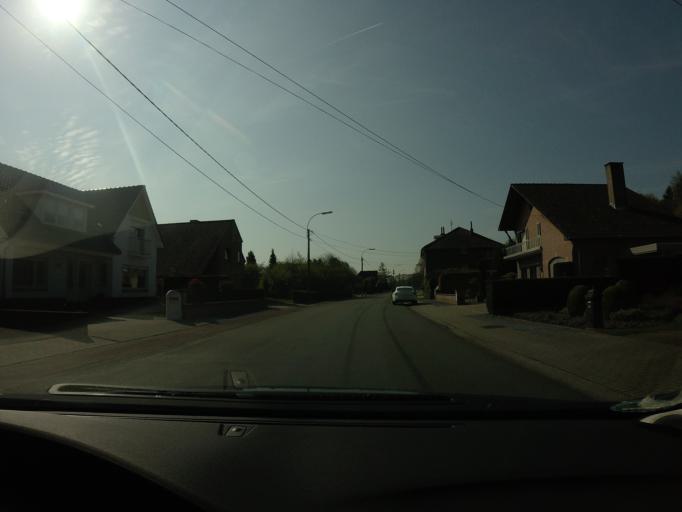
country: BE
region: Flanders
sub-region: Provincie Limburg
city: Maasmechelen
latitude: 50.9370
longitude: 5.6807
